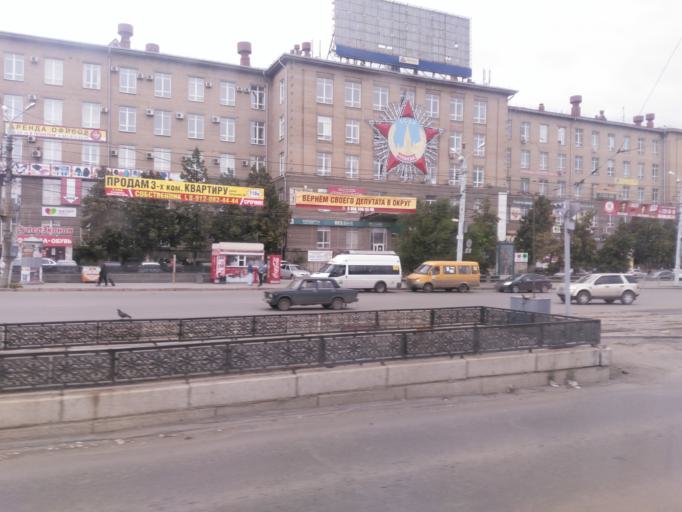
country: RU
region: Chelyabinsk
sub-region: Gorod Chelyabinsk
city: Chelyabinsk
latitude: 55.1844
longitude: 61.3984
